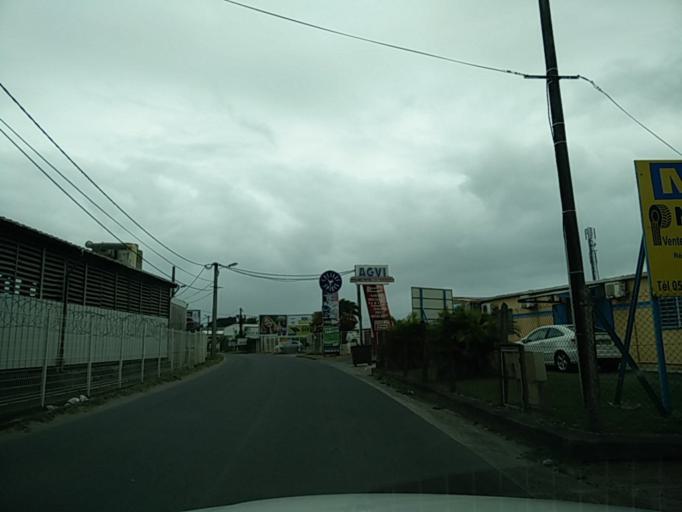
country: GP
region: Guadeloupe
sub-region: Guadeloupe
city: Pointe-a-Pitre
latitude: 16.2532
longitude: -61.5601
